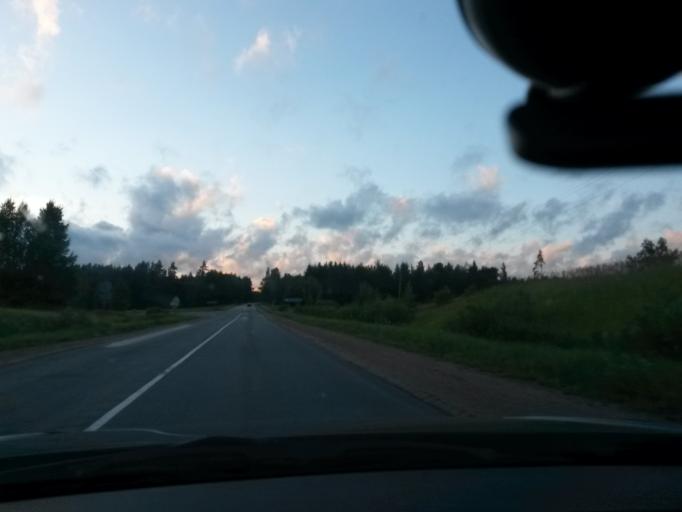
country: LV
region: Jekabpils Rajons
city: Jekabpils
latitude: 56.6919
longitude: 25.9835
